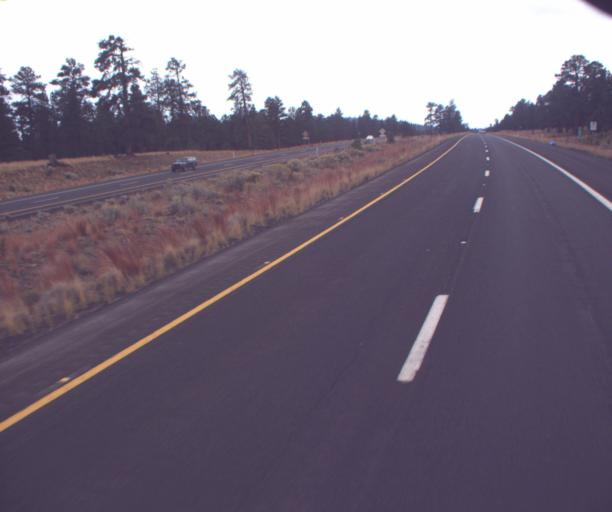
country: US
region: Arizona
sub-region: Coconino County
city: Flagstaff
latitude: 35.3802
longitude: -111.5805
